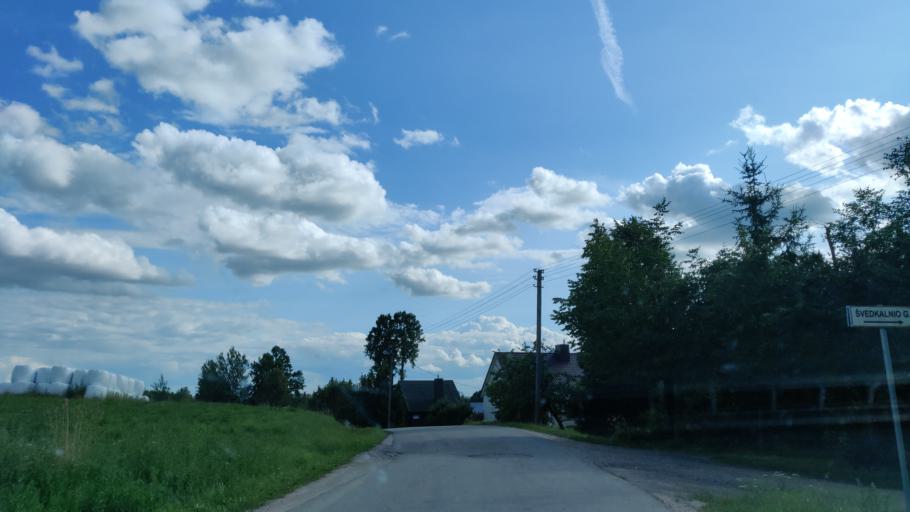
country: LT
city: Varniai
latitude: 55.5980
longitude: 22.3110
